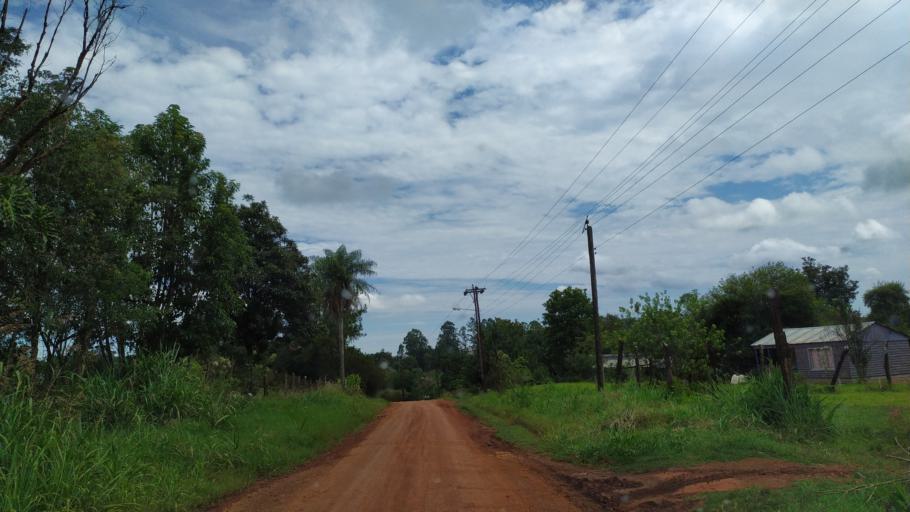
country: AR
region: Misiones
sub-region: Departamento de Eldorado
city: Eldorado
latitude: -26.5181
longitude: -54.5939
